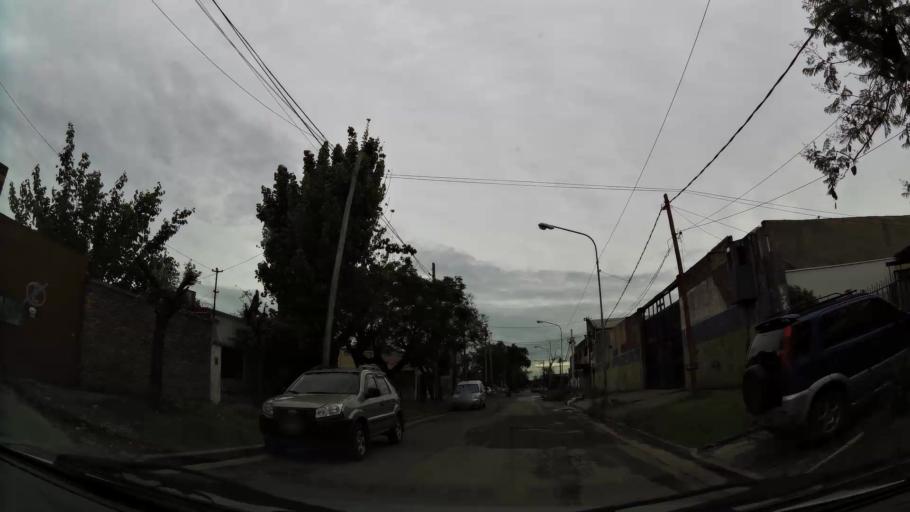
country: AR
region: Buenos Aires
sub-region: Partido de Lanus
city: Lanus
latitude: -34.7221
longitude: -58.3709
